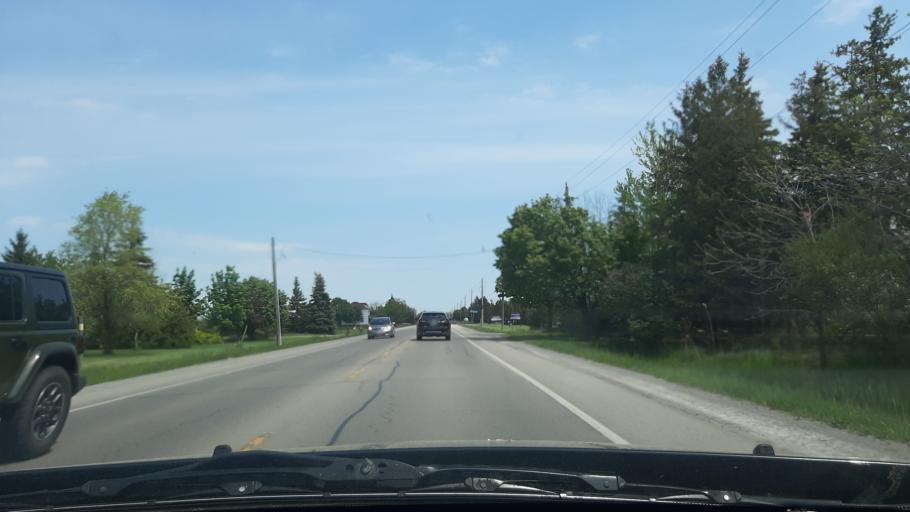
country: CA
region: Ontario
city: Thorold
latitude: 43.2046
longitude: -79.1446
